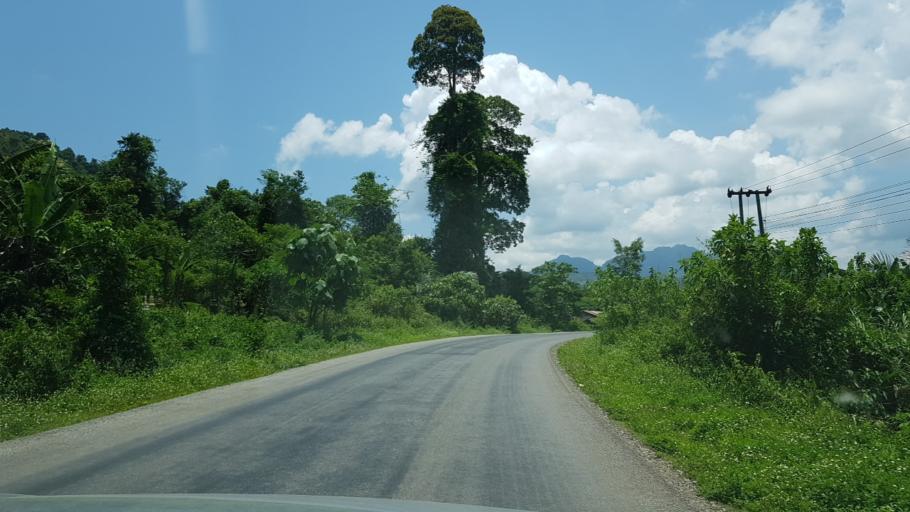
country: LA
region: Vientiane
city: Muang Kasi
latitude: 19.1273
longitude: 102.2618
